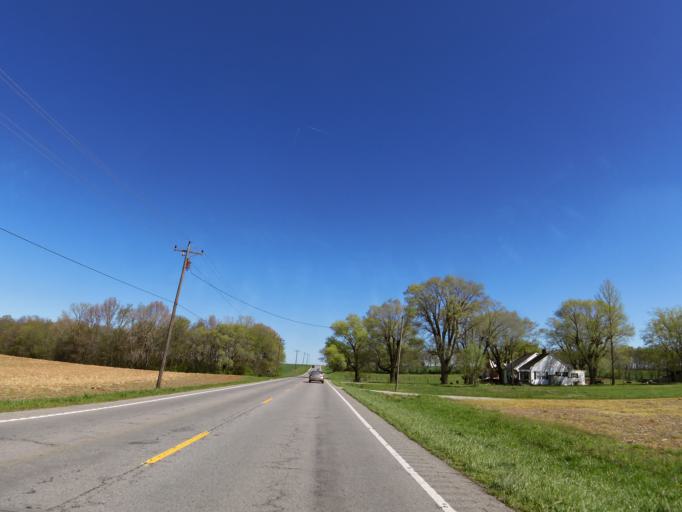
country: US
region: Tennessee
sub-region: Robertson County
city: Springfield
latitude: 36.5815
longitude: -86.8557
